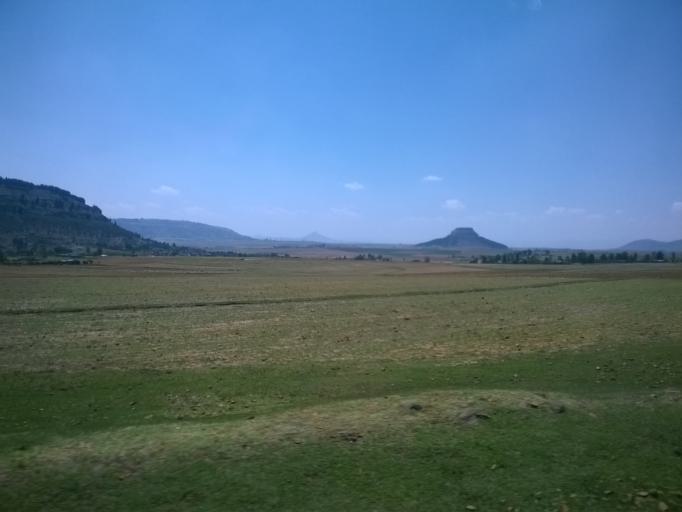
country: LS
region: Leribe
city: Maputsoe
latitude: -28.9661
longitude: 27.9633
